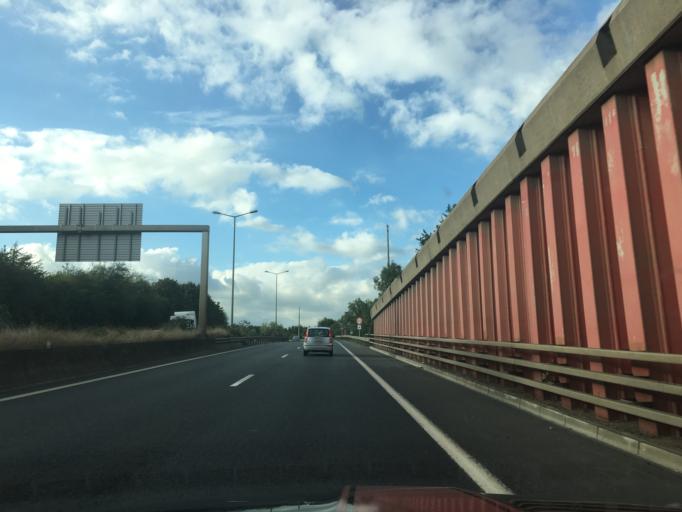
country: LU
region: Luxembourg
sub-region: Canton d'Esch-sur-Alzette
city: Mondercange
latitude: 49.5262
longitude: 5.9670
